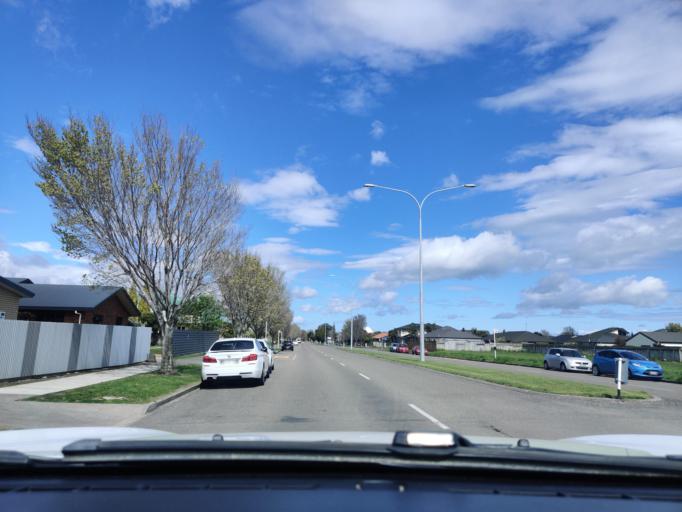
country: NZ
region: Manawatu-Wanganui
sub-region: Palmerston North City
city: Palmerston North
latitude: -40.3240
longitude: 175.6127
